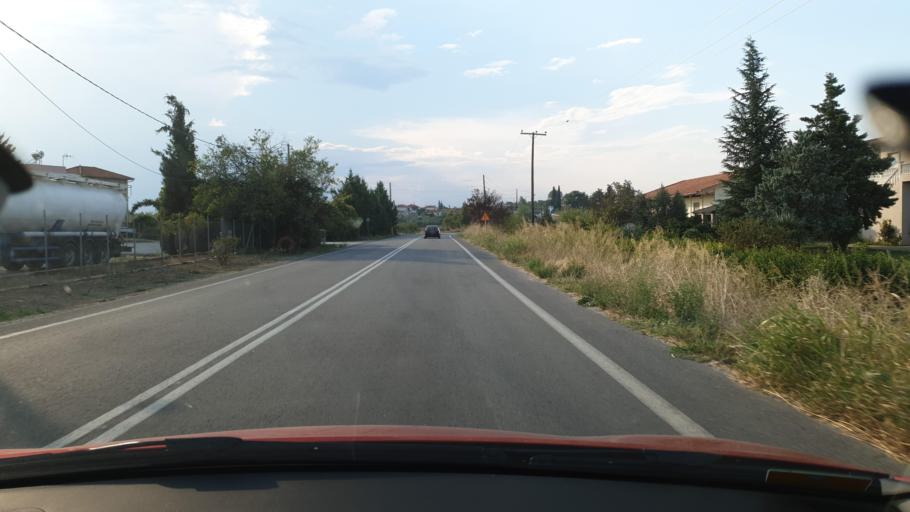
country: GR
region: Thessaly
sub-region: Nomos Magnisias
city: Almyros
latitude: 39.1585
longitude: 22.8004
